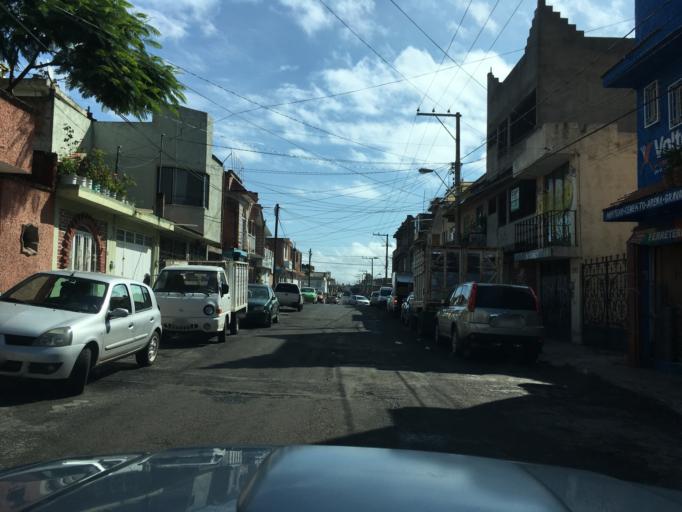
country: MX
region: Michoacan
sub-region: Tarimbaro
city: Fraccionamiento Metropolis II
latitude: 19.7226
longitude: -101.2312
